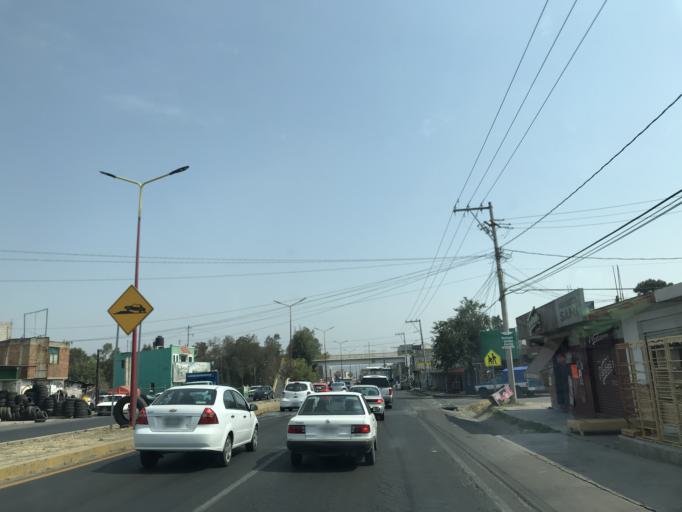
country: MX
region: Tlaxcala
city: La Magdalena Tlaltelulco
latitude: 19.2906
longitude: -98.1951
